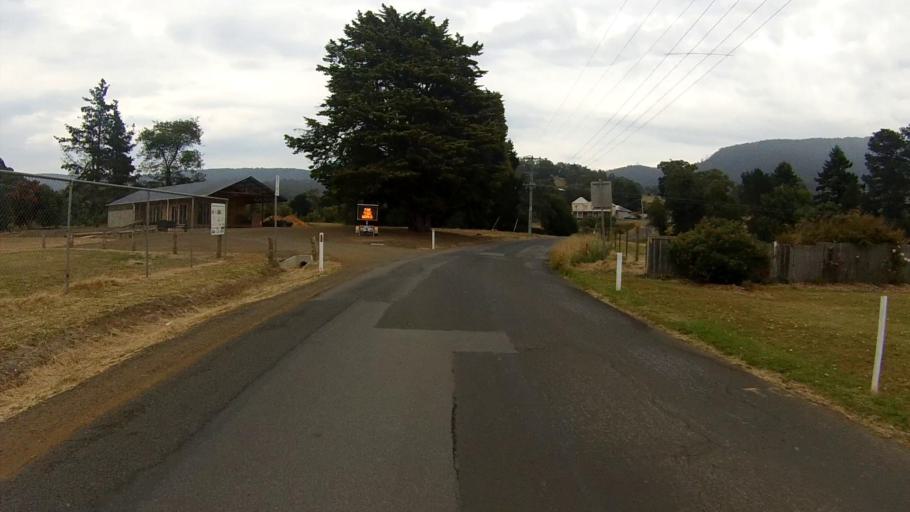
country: AU
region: Tasmania
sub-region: Kingborough
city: Kettering
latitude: -43.1603
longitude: 147.2356
